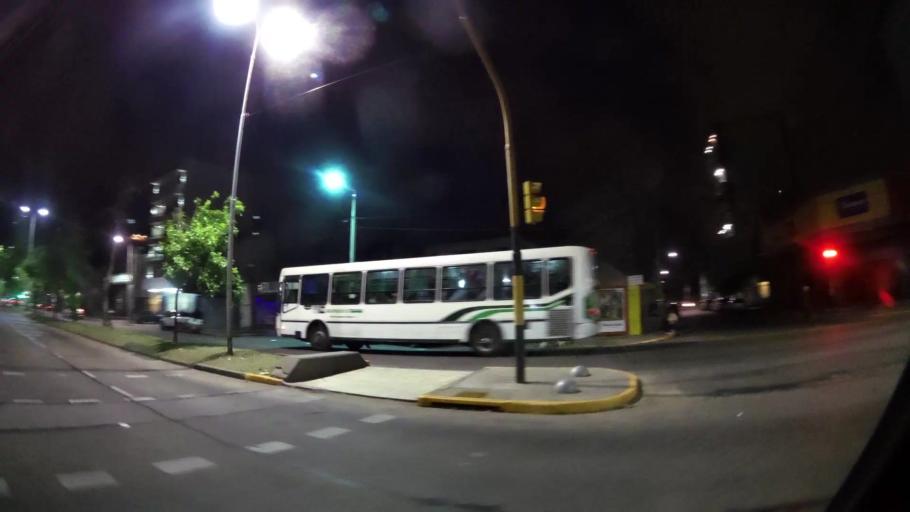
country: AR
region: Buenos Aires
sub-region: Partido de Avellaneda
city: Avellaneda
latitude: -34.7022
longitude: -58.3199
